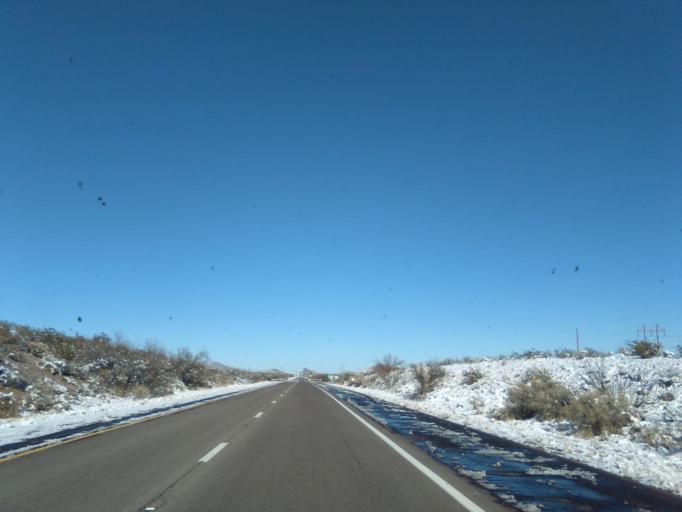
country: US
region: New Mexico
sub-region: Socorro County
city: Socorro
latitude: 33.7075
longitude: -107.0423
